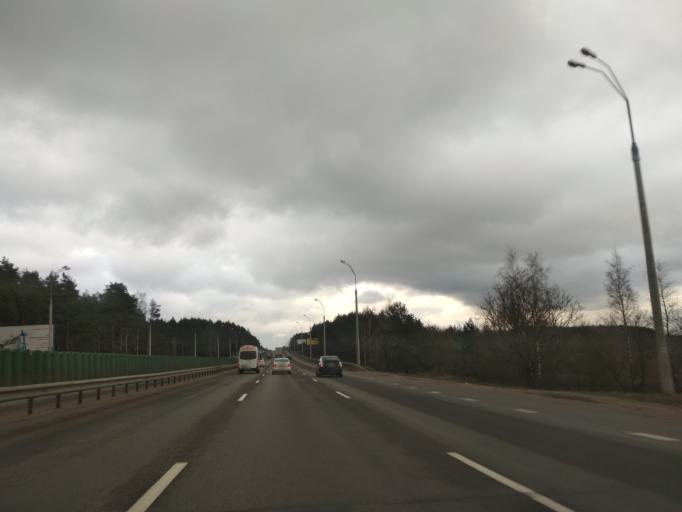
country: BY
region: Minsk
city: Vyaliki Trastsyanets
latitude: 53.8325
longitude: 27.7376
